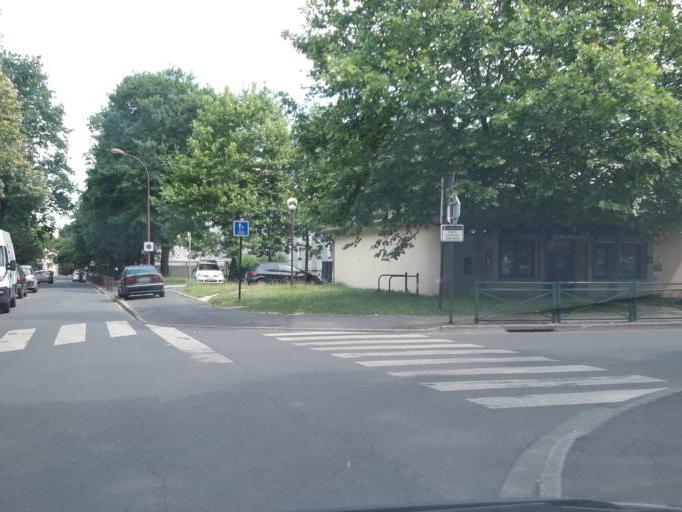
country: FR
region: Ile-de-France
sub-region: Departement de l'Essonne
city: Fleury-Merogis
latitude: 48.6416
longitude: 2.3442
